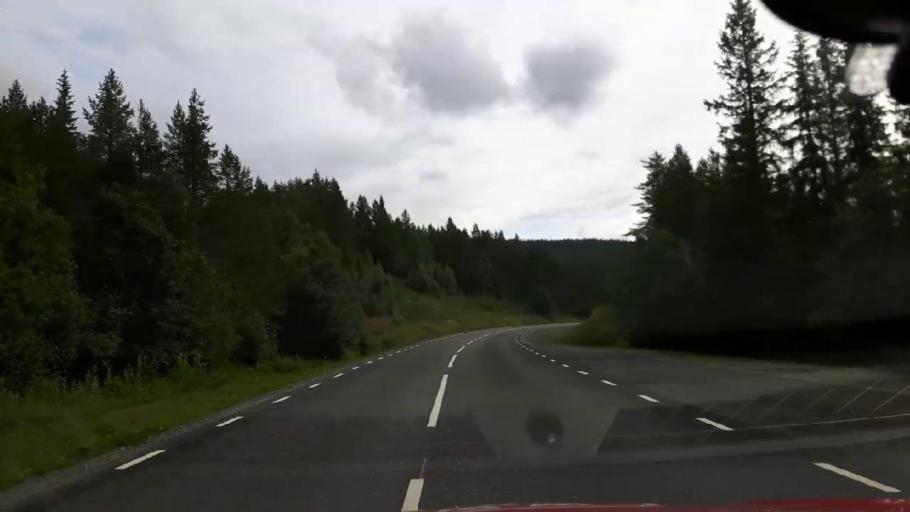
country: NO
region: Nord-Trondelag
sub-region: Lierne
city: Sandvika
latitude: 64.6358
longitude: 14.1402
